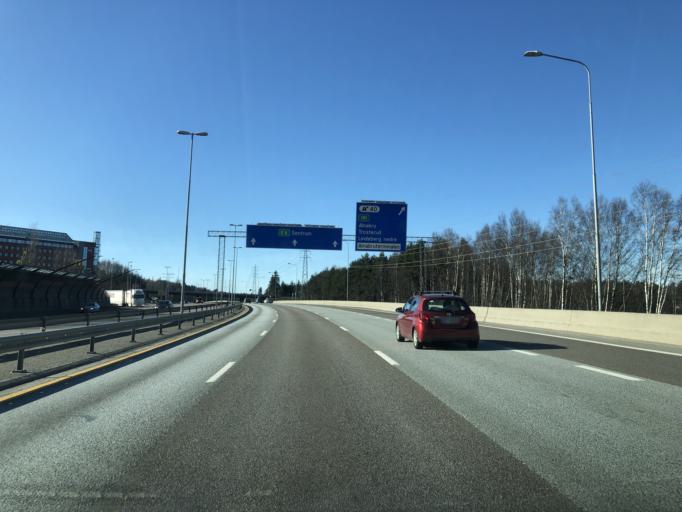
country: NO
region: Akershus
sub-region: Lorenskog
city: Kjenn
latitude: 59.9326
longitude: 10.8700
